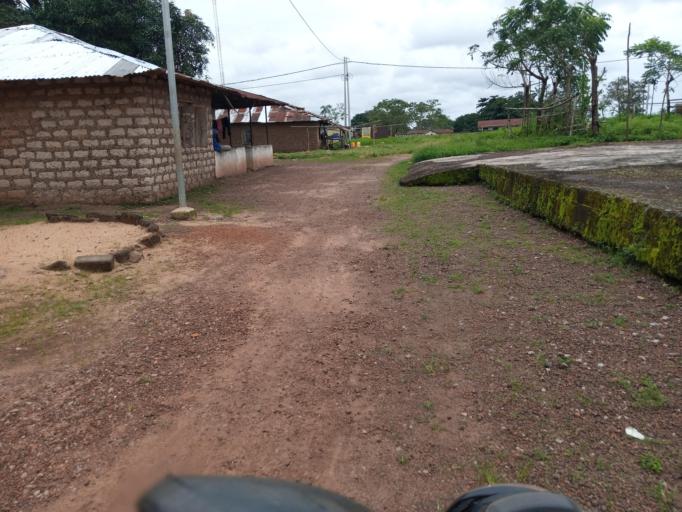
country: SL
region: Southern Province
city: Largo
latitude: 8.2003
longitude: -12.0609
